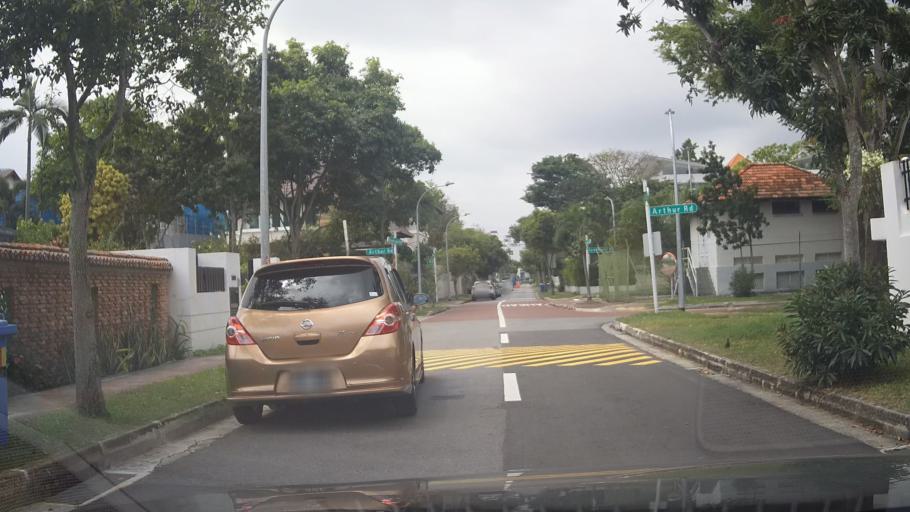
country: SG
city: Singapore
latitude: 1.3034
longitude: 103.8886
